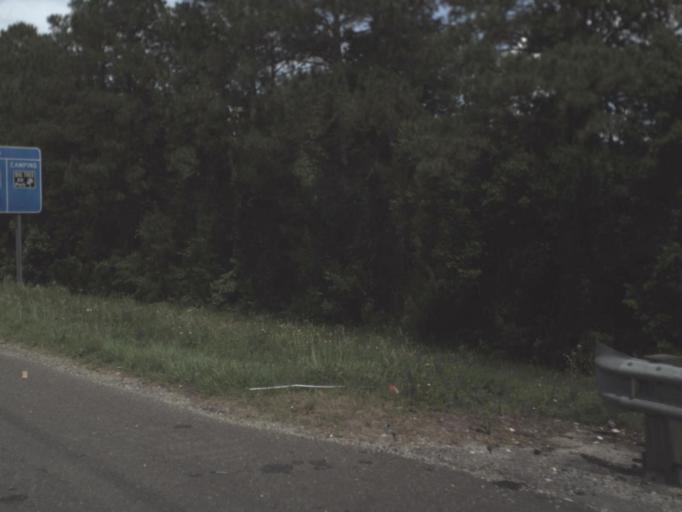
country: US
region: Florida
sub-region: Nassau County
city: Nassau Village-Ratliff
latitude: 30.4235
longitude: -81.7336
